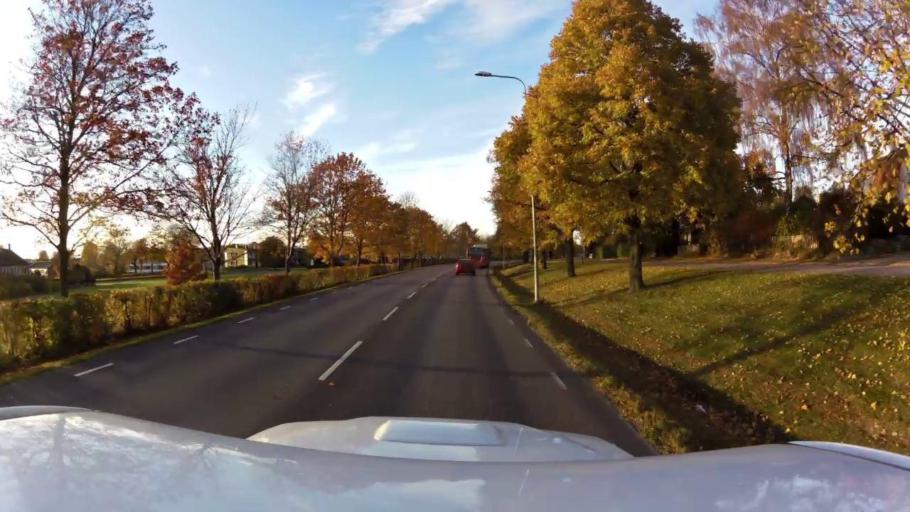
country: SE
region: OEstergoetland
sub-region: Linkopings Kommun
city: Linkoping
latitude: 58.3893
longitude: 15.6503
